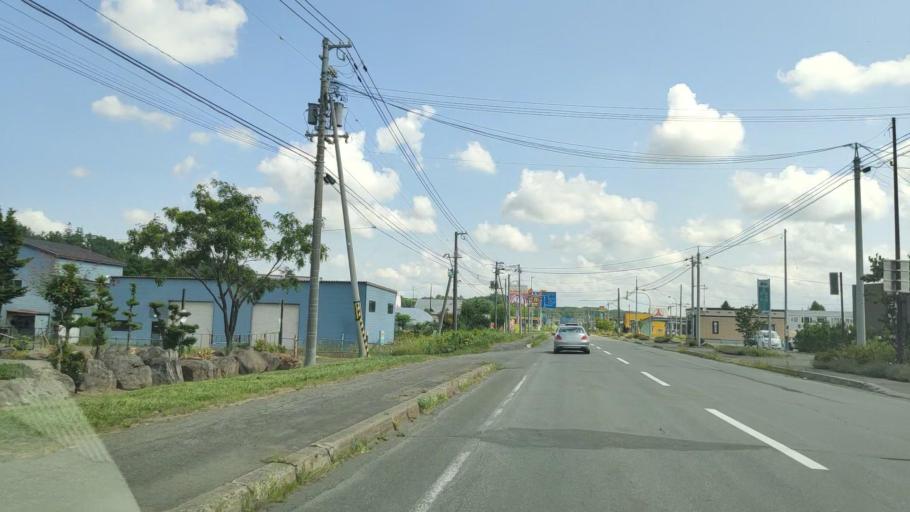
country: JP
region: Hokkaido
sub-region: Asahikawa-shi
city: Asahikawa
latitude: 43.5943
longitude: 142.4589
